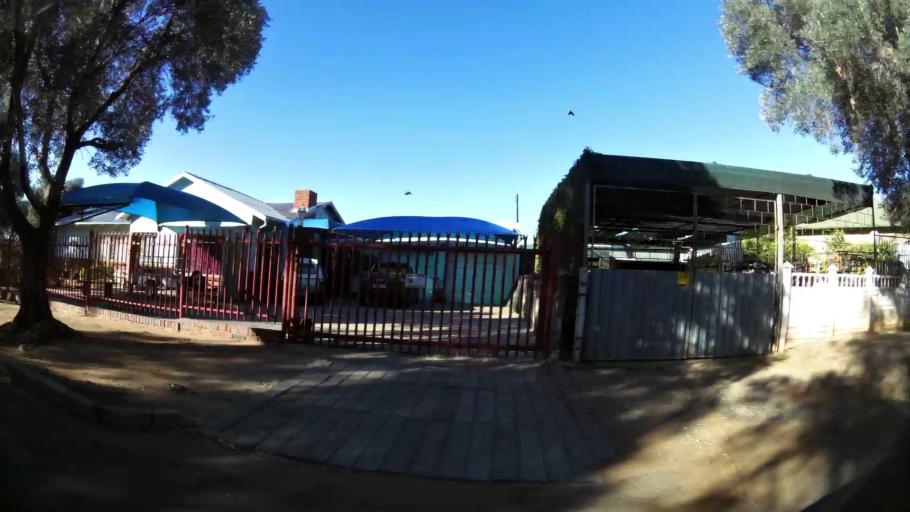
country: ZA
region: Northern Cape
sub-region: Frances Baard District Municipality
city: Kimberley
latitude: -28.7488
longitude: 24.7887
